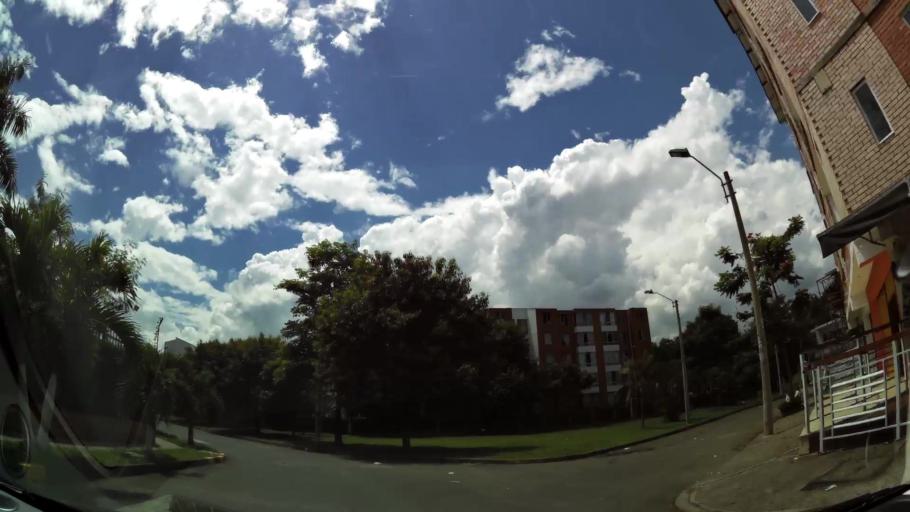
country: CO
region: Valle del Cauca
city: Cali
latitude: 3.3843
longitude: -76.5191
